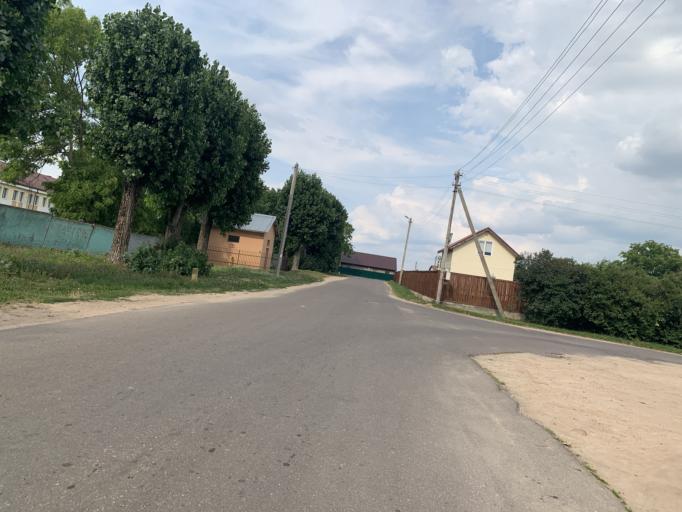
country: BY
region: Minsk
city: Nyasvizh
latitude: 53.2096
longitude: 26.6892
